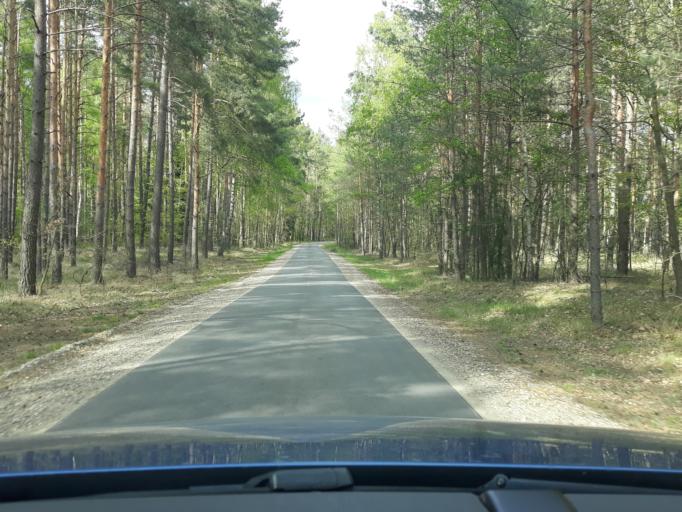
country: PL
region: Pomeranian Voivodeship
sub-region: Powiat czluchowski
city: Czluchow
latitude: 53.7230
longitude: 17.3344
